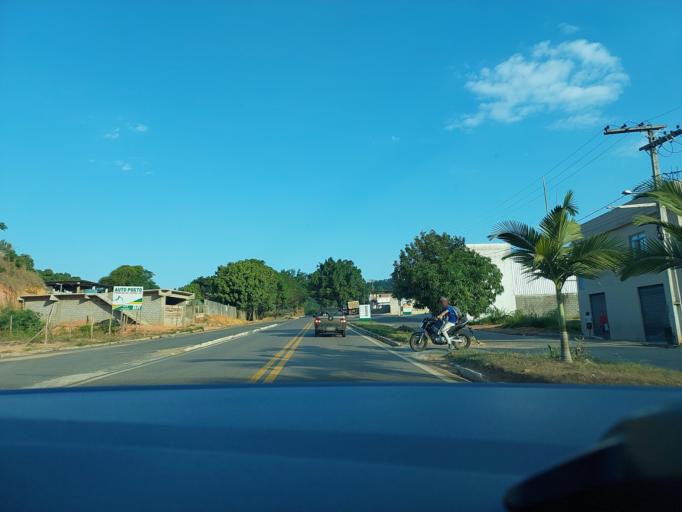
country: BR
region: Minas Gerais
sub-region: Muriae
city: Muriae
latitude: -21.1073
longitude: -42.4567
